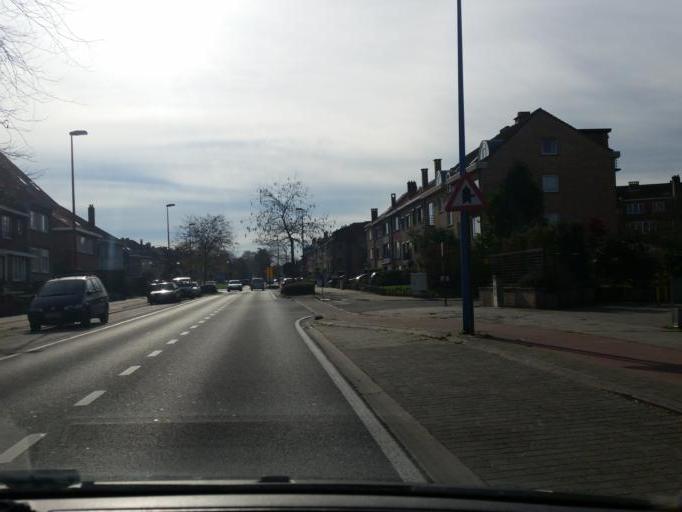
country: BE
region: Flanders
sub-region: Provincie Vlaams-Brabant
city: Grimbergen
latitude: 50.9118
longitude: 4.3665
